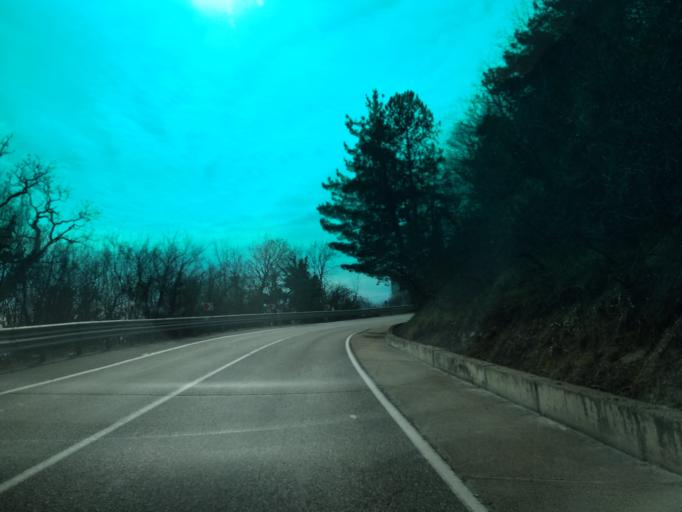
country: RU
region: Krasnodarskiy
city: Shepsi
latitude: 44.0482
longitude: 39.1335
